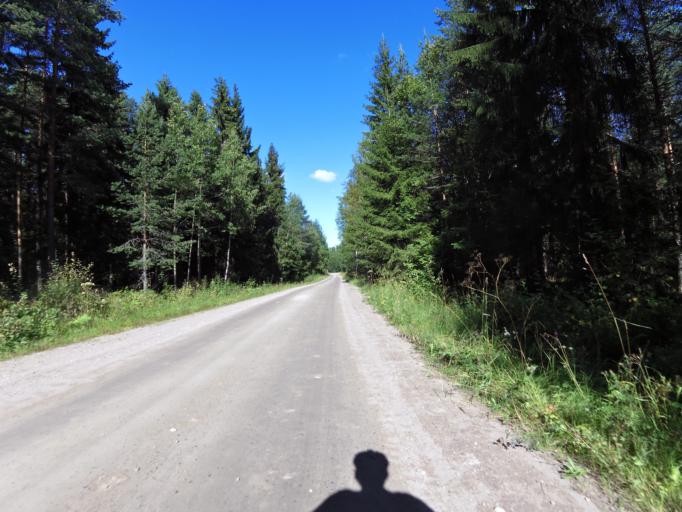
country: SE
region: Gaevleborg
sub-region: Hofors Kommun
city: Hofors
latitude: 60.5102
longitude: 16.4082
